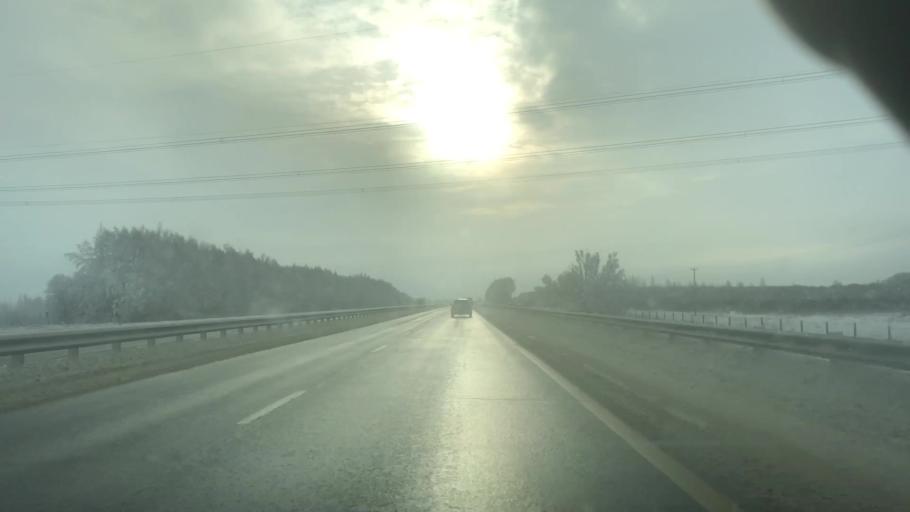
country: RU
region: Tula
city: Venev
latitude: 54.2902
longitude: 38.1594
